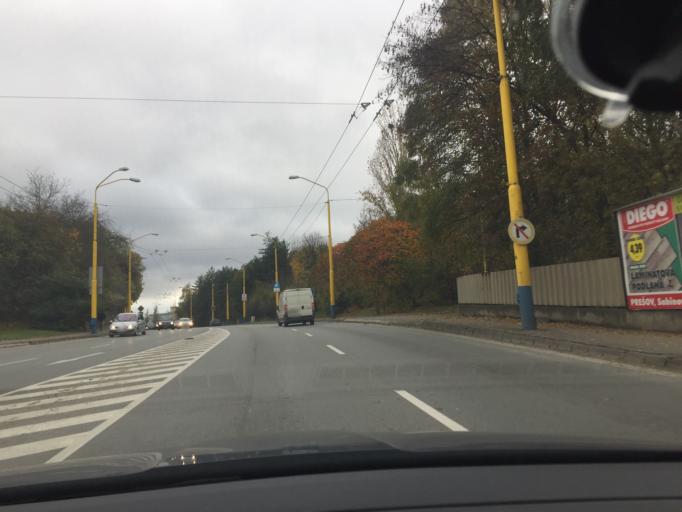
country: SK
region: Presovsky
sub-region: Okres Presov
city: Presov
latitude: 49.0053
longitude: 21.2453
